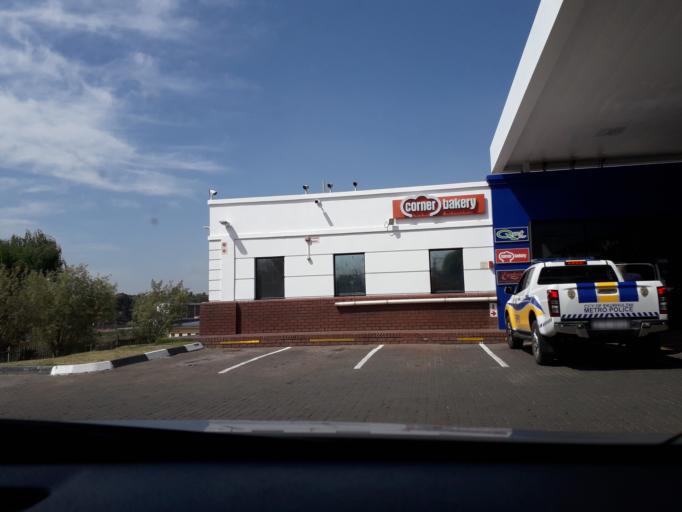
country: ZA
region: Gauteng
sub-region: Ekurhuleni Metropolitan Municipality
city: Tembisa
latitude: -26.0676
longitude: 28.2353
